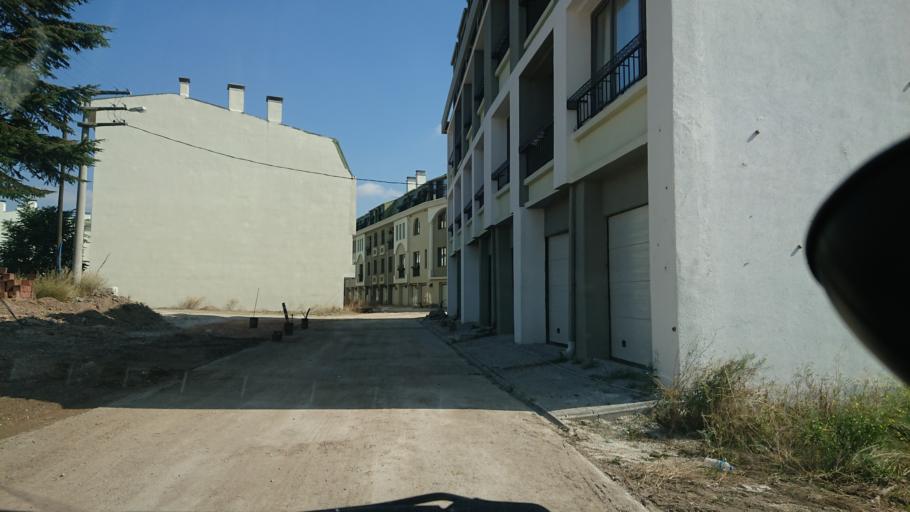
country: TR
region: Eskisehir
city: Eskisehir
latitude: 39.7539
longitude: 30.4758
